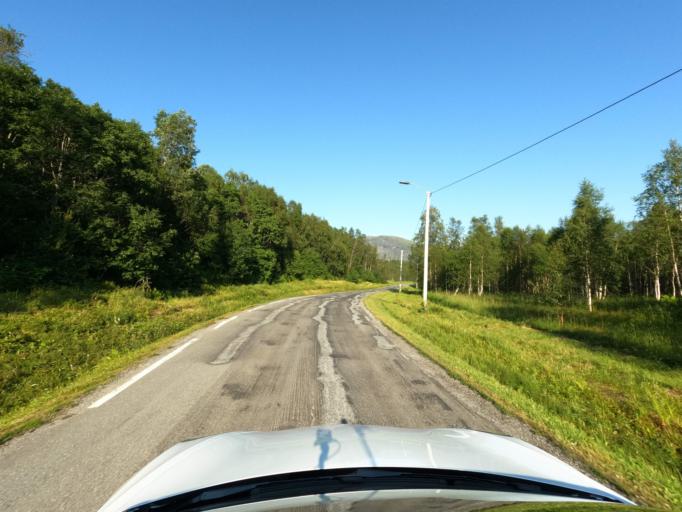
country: NO
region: Troms
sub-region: Gratangen
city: Gratangen
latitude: 68.5610
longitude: 17.7047
